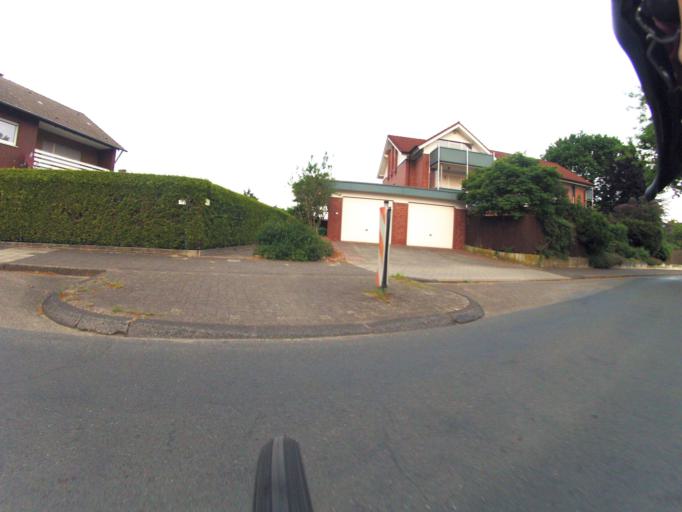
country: DE
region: North Rhine-Westphalia
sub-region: Regierungsbezirk Munster
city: Mettingen
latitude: 52.2655
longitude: 7.7858
